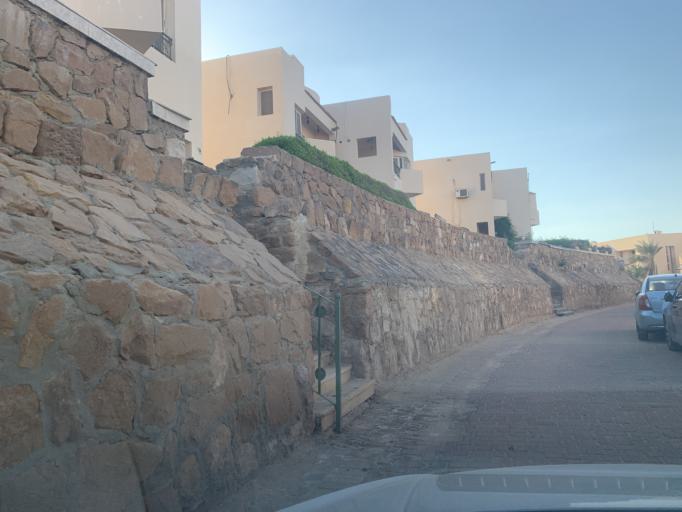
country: EG
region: As Suways
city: Ain Sukhna
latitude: 29.3734
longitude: 32.5724
